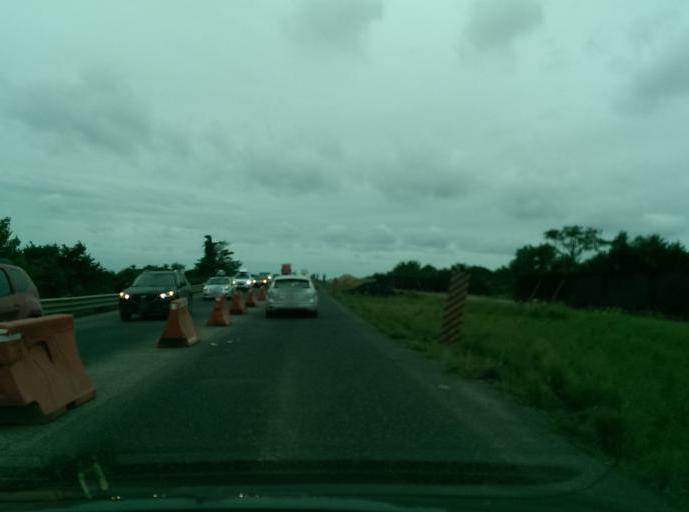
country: MX
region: Veracruz
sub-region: Jose Azueta
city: Tesechoacan
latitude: 18.1935
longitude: -95.5936
